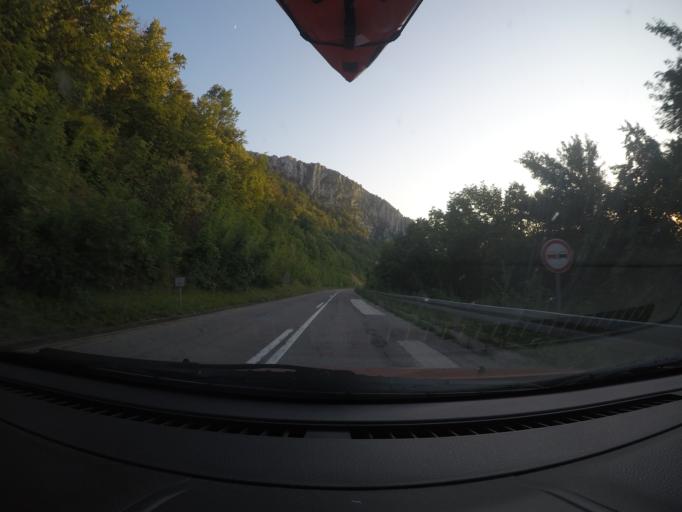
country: RO
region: Mehedinti
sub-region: Comuna Dubova
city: Dubova
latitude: 44.6353
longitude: 22.3036
